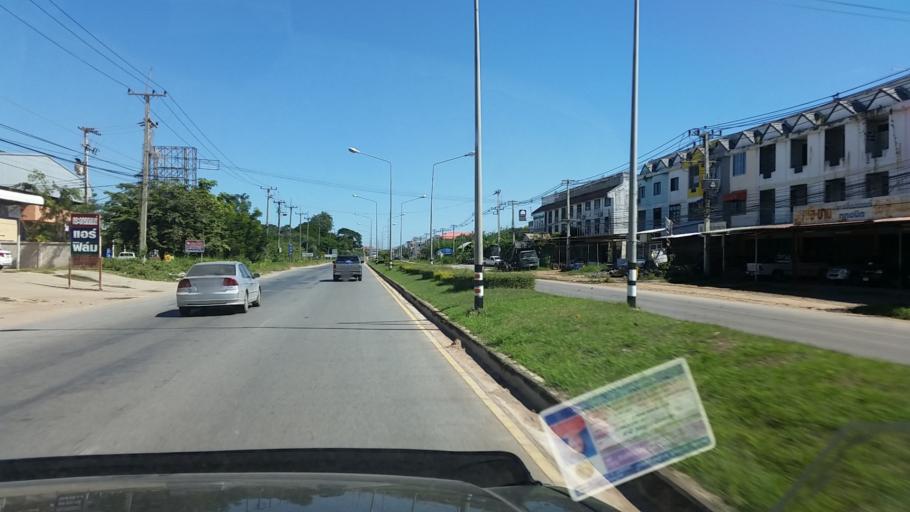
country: TH
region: Chaiyaphum
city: Chaiyaphum
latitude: 15.7944
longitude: 102.0084
